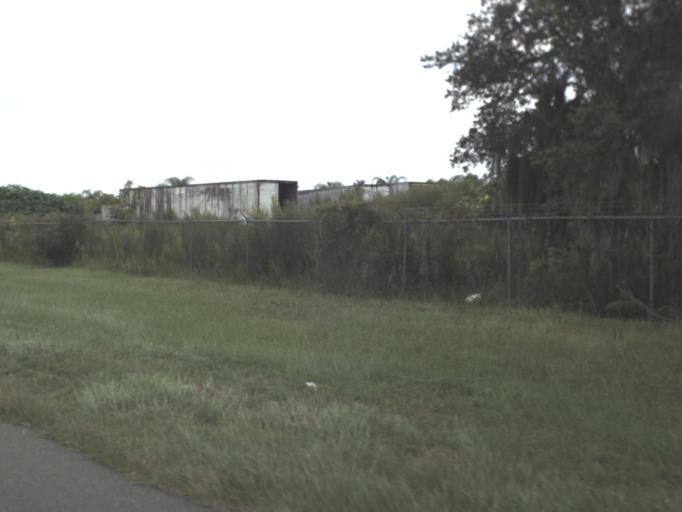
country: US
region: Florida
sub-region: Hillsborough County
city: Wimauma
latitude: 27.7100
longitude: -82.2686
